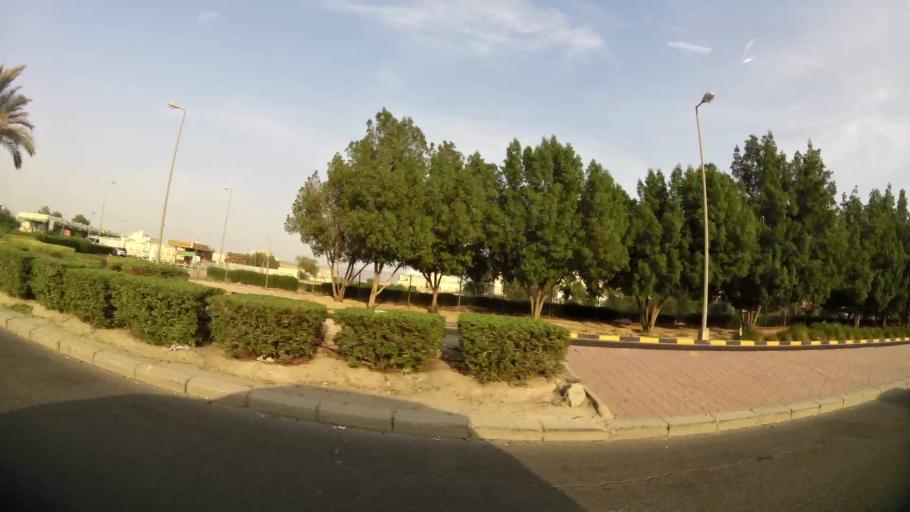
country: KW
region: Mubarak al Kabir
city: Sabah as Salim
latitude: 29.2292
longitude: 48.0532
